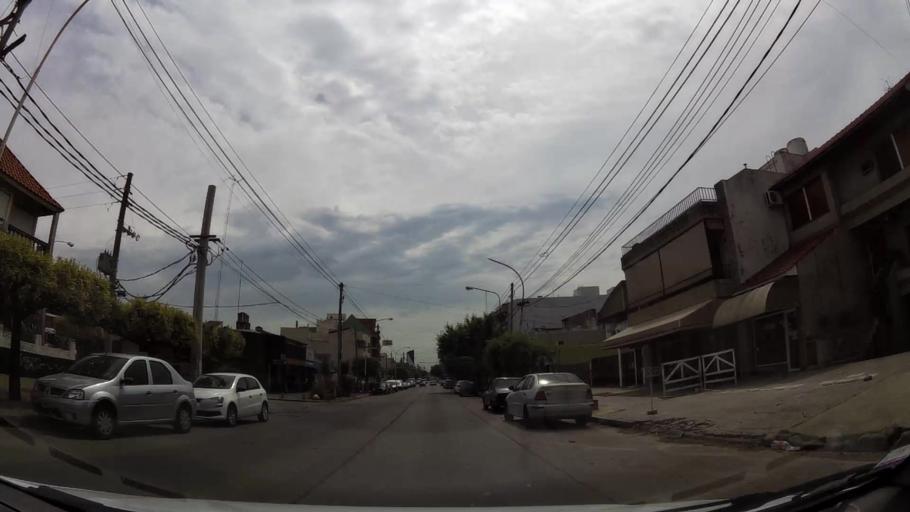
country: AR
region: Buenos Aires F.D.
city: Villa Lugano
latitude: -34.6931
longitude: -58.5013
